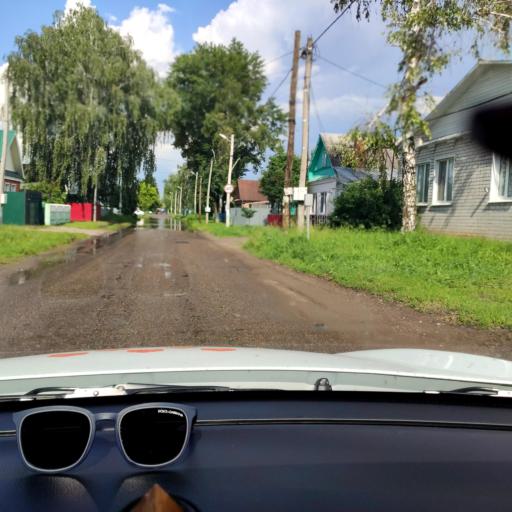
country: RU
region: Tatarstan
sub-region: Zelenodol'skiy Rayon
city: Vasil'yevo
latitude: 55.8322
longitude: 48.7141
